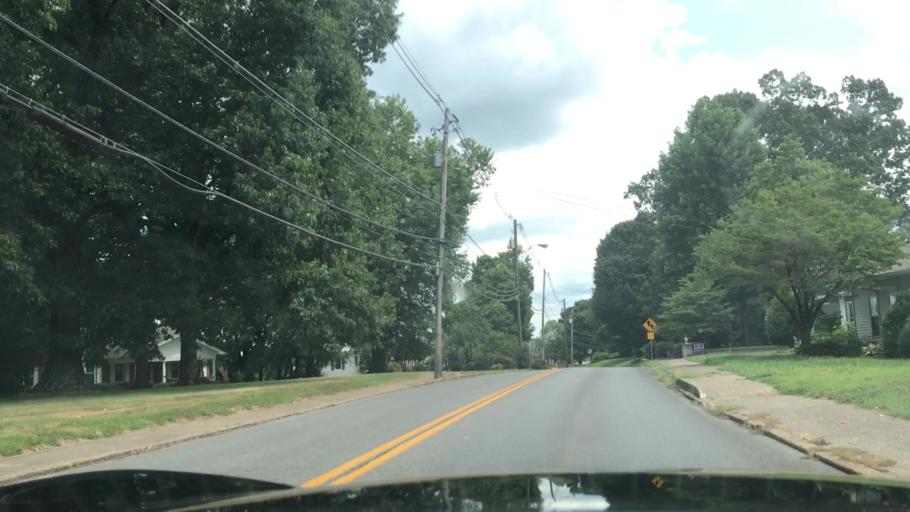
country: US
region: Kentucky
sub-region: Muhlenberg County
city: Greenville
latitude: 37.2044
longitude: -87.1721
